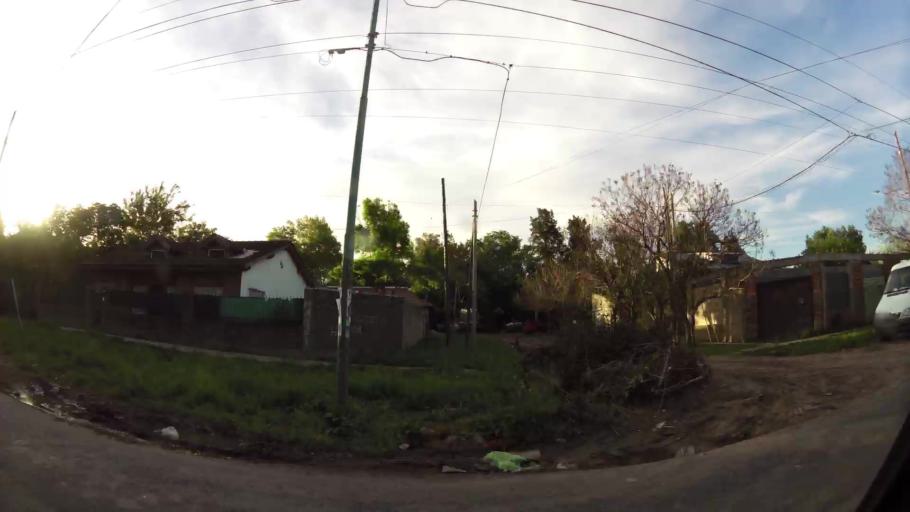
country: AR
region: Buenos Aires
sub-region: Partido de Quilmes
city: Quilmes
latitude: -34.7925
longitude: -58.1904
